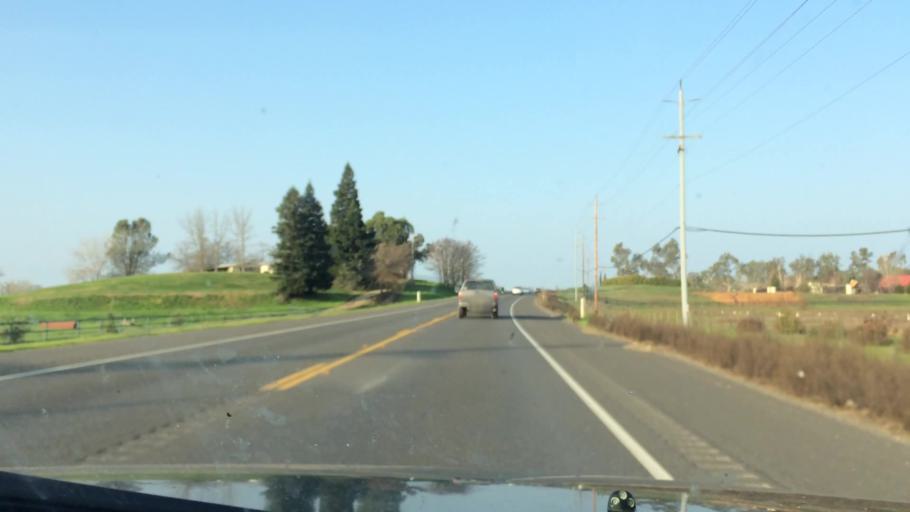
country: US
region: California
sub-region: Sacramento County
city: Rancho Murieta
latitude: 38.4967
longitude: -121.1094
